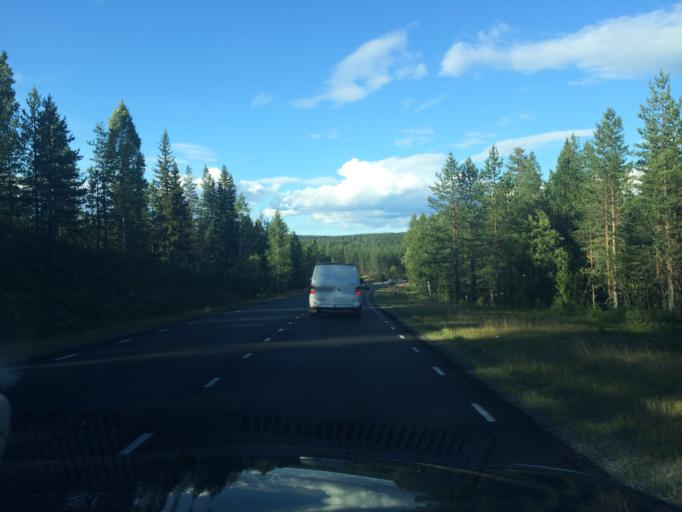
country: NO
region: Hedmark
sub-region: Trysil
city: Innbygda
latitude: 61.0843
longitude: 11.9830
